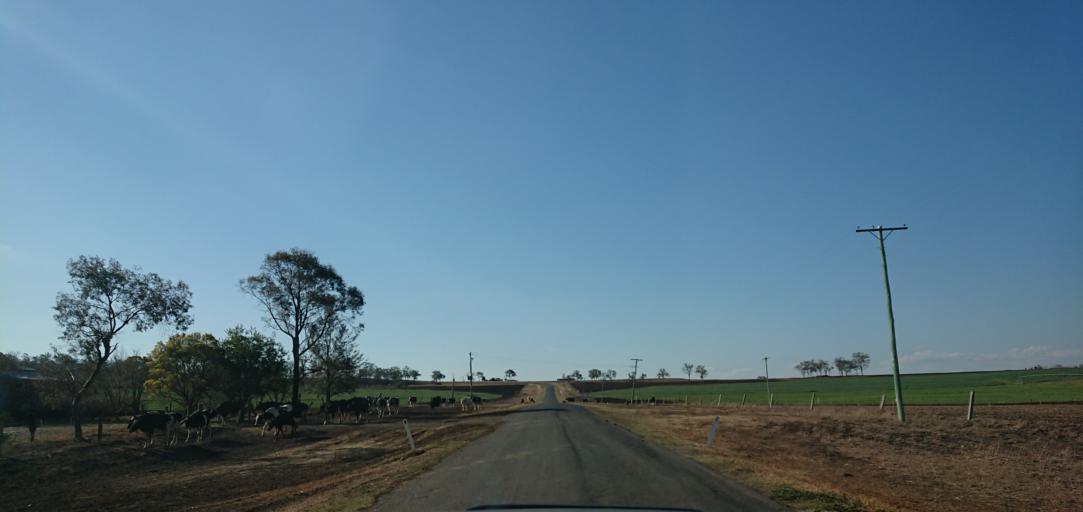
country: AU
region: Queensland
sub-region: Toowoomba
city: Westbrook
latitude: -27.7075
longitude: 151.7163
